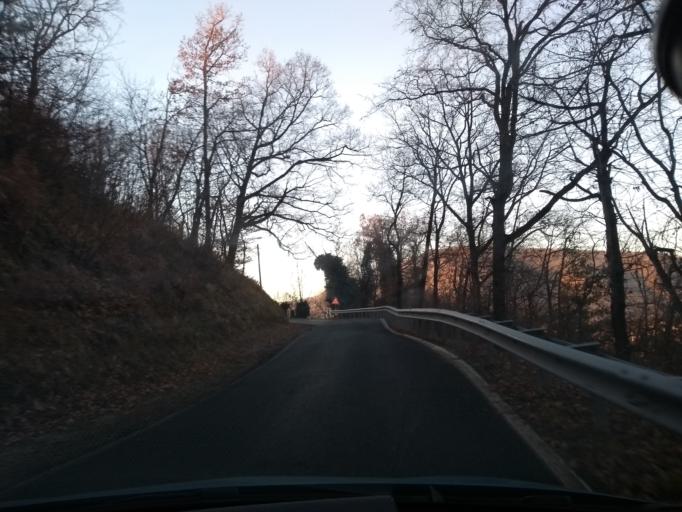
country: IT
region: Piedmont
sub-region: Provincia di Torino
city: Balangero
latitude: 45.2746
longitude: 7.5278
